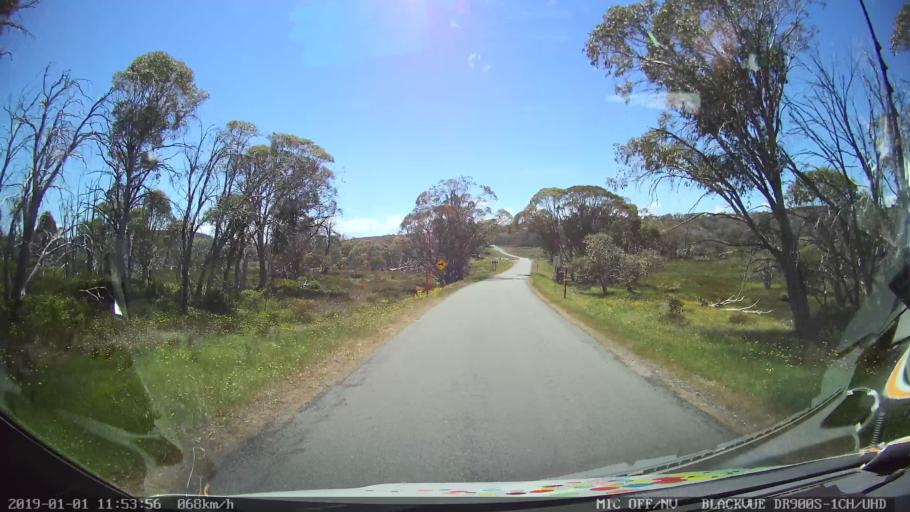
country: AU
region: New South Wales
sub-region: Snowy River
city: Jindabyne
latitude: -35.8919
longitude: 148.4448
